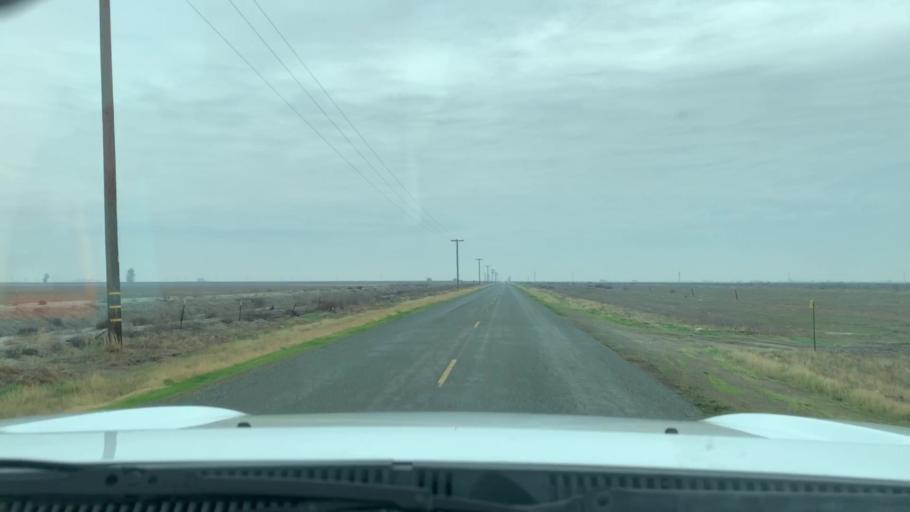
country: US
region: California
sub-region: Tulare County
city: Alpaugh
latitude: 35.7610
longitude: -119.4859
